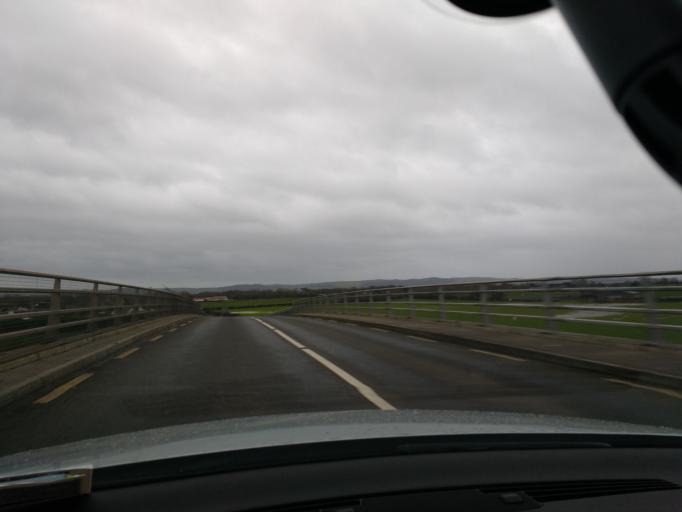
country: IE
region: Munster
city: Thurles
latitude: 52.6717
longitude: -7.6930
